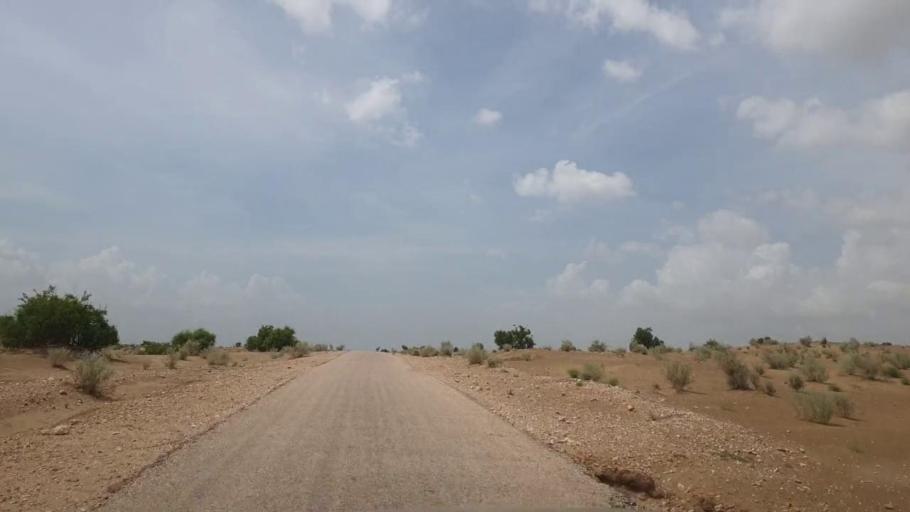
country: PK
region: Sindh
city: Kot Diji
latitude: 27.2049
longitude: 69.0857
